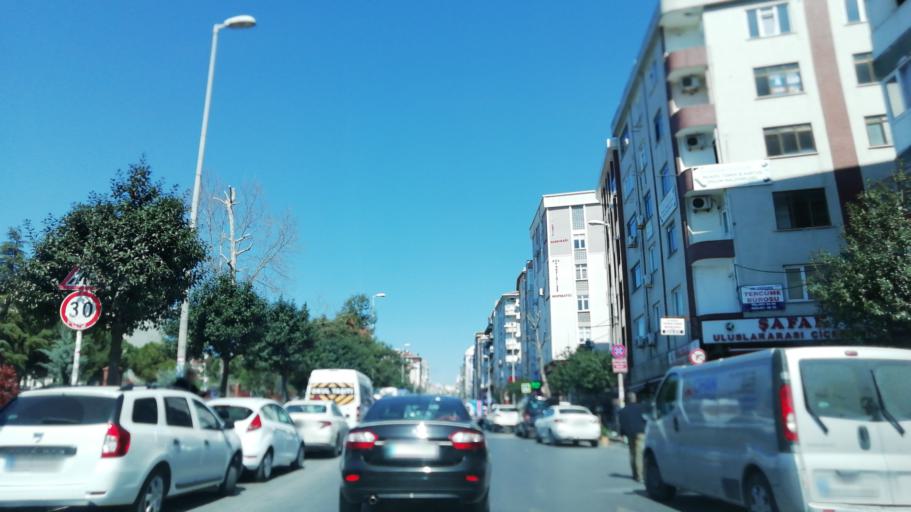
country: TR
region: Istanbul
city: Bahcelievler
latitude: 40.9951
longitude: 28.8351
